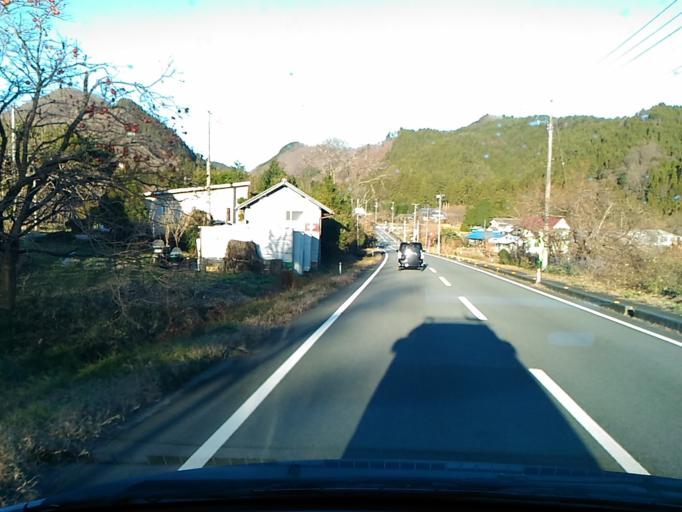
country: JP
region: Ibaraki
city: Kitaibaraki
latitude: 36.9306
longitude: 140.6912
